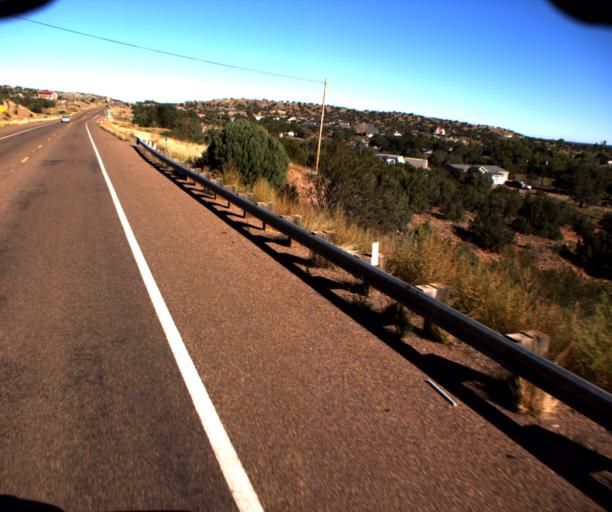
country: US
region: Arizona
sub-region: Navajo County
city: Taylor
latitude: 34.4033
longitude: -110.0742
